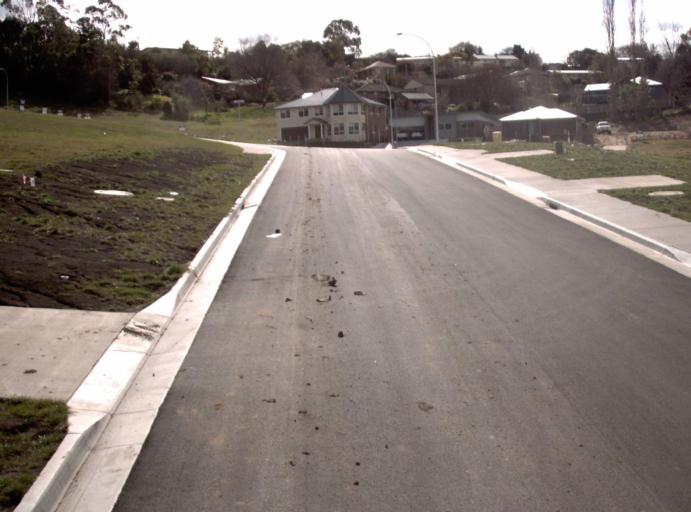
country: AU
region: Tasmania
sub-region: Launceston
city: Newstead
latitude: -41.4532
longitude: 147.1686
